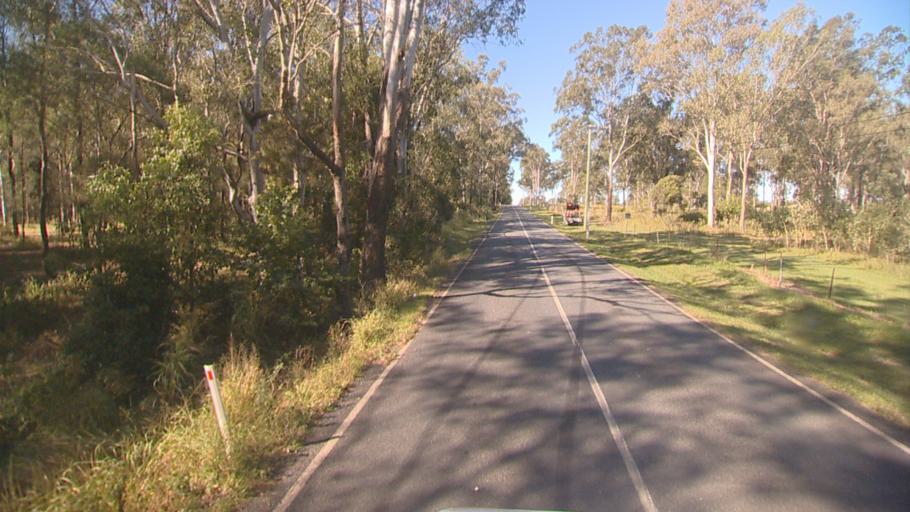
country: AU
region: Queensland
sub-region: Logan
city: Waterford West
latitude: -27.7168
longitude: 153.1342
